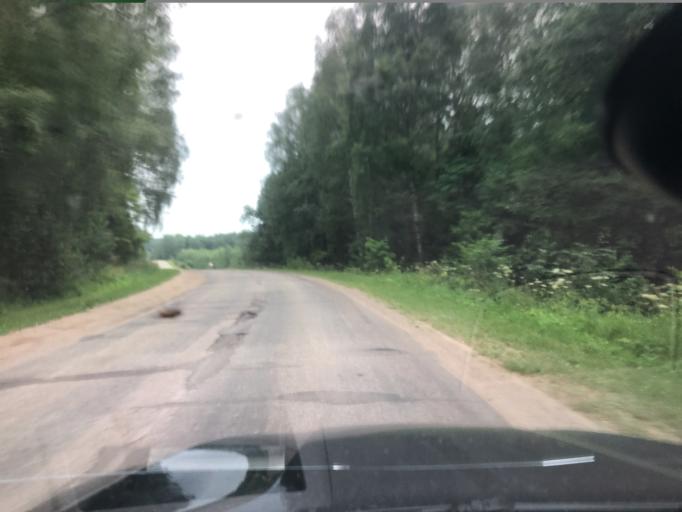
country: RU
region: Jaroslavl
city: Petrovsk
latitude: 56.9851
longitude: 39.2033
